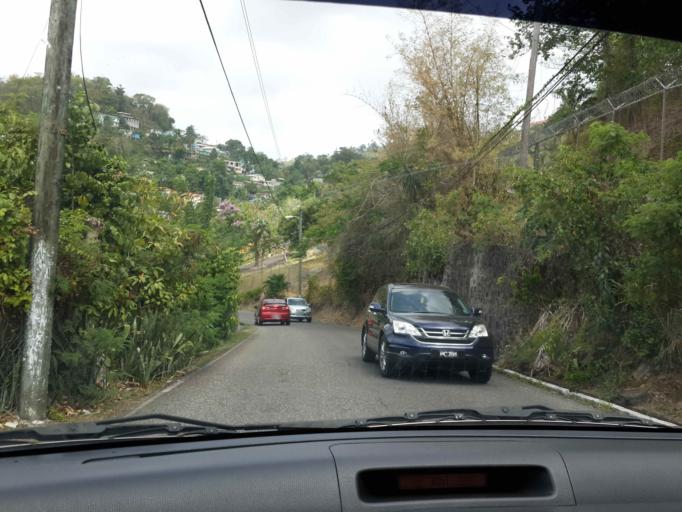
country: LC
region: Castries Quarter
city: Castries
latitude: 14.0064
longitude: -60.9942
